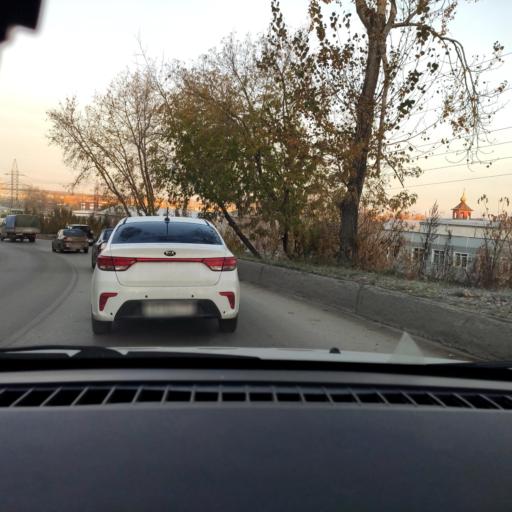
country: RU
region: Perm
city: Perm
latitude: 58.0711
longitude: 56.3517
